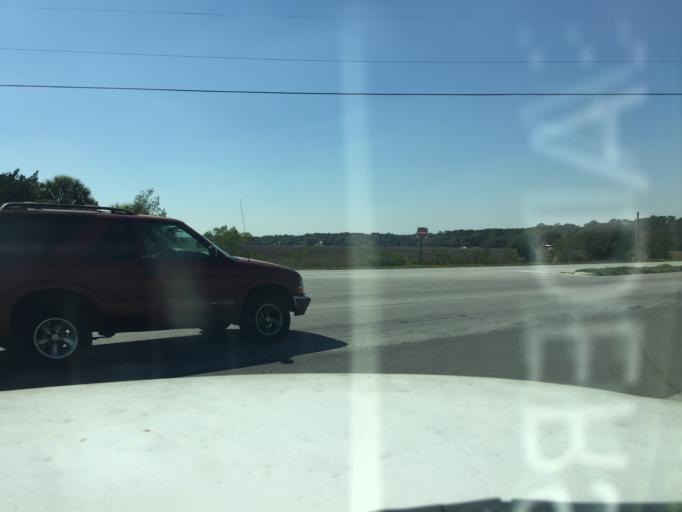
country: US
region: Georgia
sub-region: Chatham County
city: Whitemarsh Island
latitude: 32.0227
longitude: -80.9952
